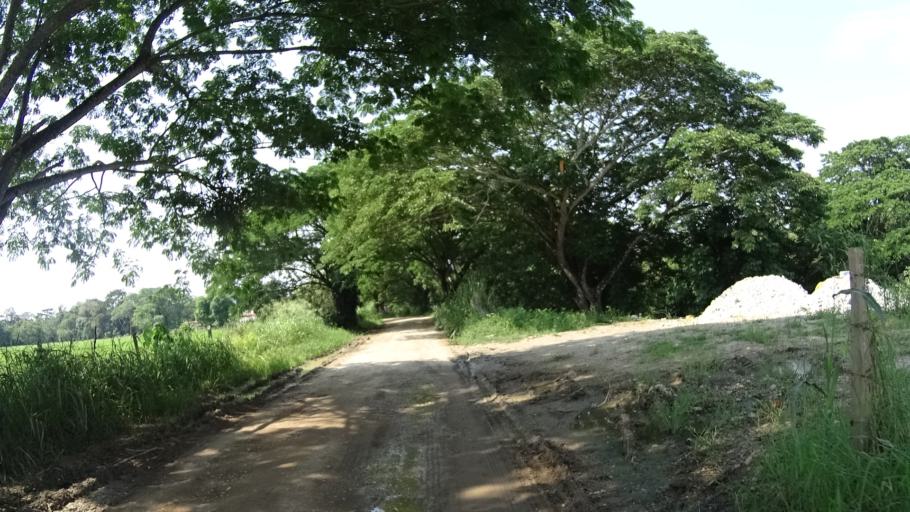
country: CO
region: Cundinamarca
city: Puerto Salgar
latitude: 5.5323
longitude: -74.6846
